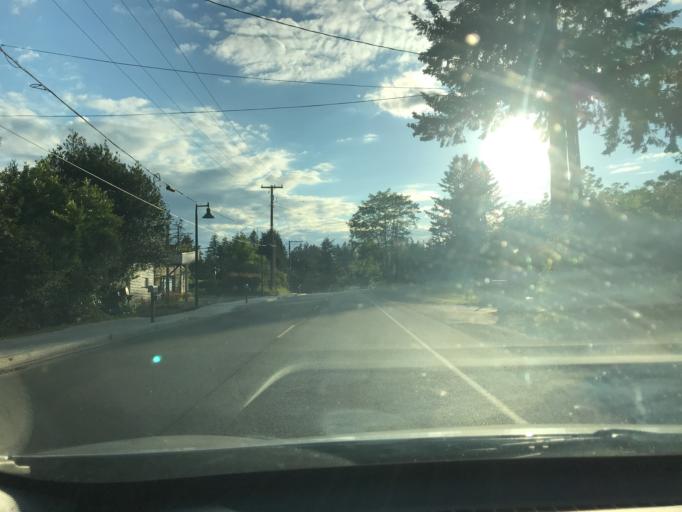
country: US
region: Washington
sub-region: King County
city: Black Diamond
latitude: 47.3122
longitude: -122.0192
